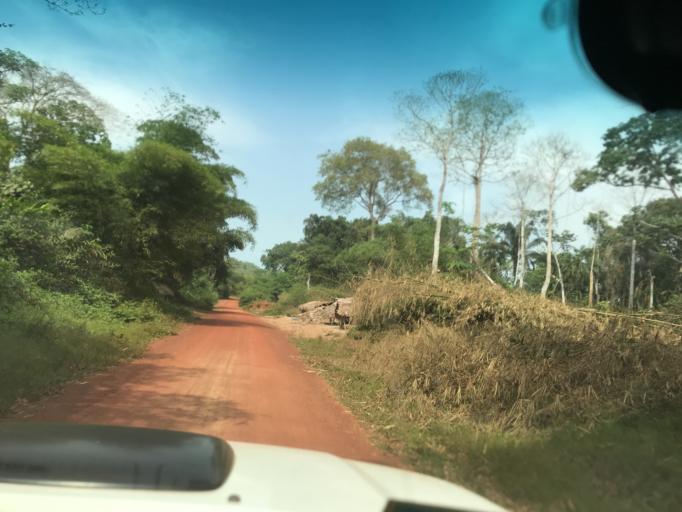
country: CD
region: Eastern Province
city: Buta
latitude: 2.8912
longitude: 24.3017
